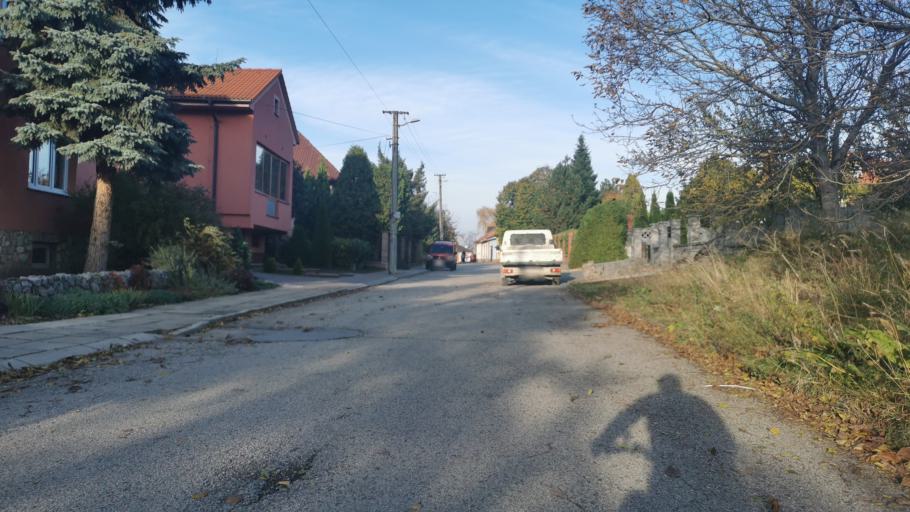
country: SK
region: Trnavsky
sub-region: Okres Skalica
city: Skalica
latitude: 48.8412
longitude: 17.2406
